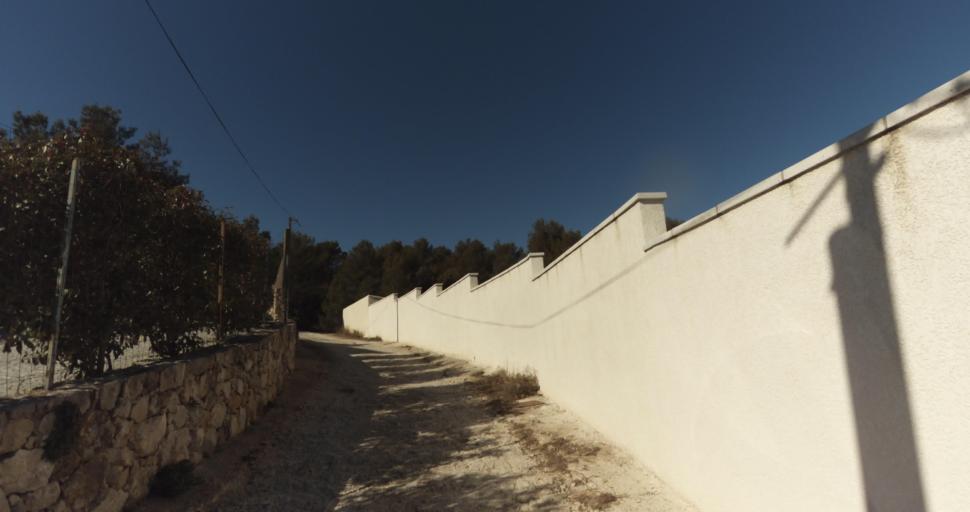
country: FR
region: Provence-Alpes-Cote d'Azur
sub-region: Departement des Bouches-du-Rhone
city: Peypin
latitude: 43.3893
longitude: 5.5702
